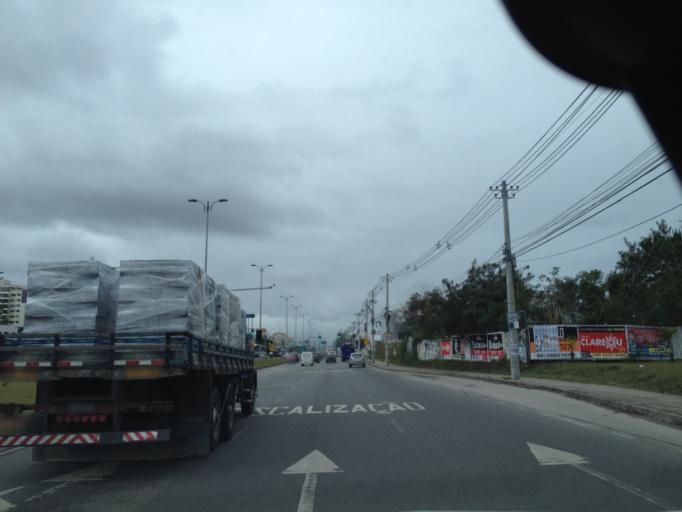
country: BR
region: Rio de Janeiro
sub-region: Nilopolis
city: Nilopolis
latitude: -23.0193
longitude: -43.4850
